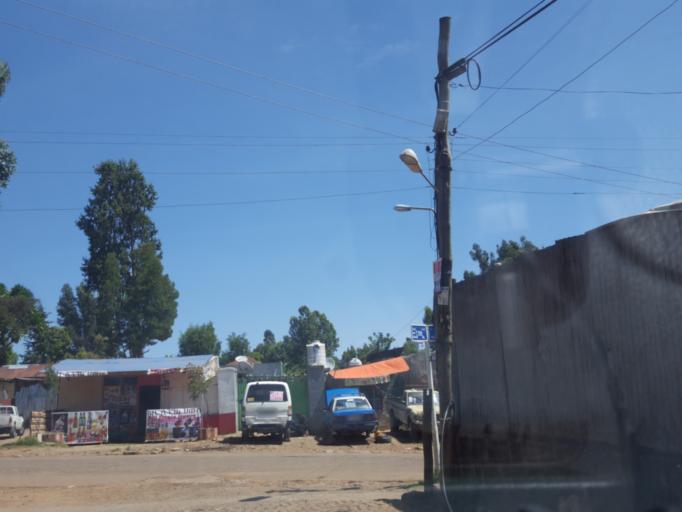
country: ET
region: Adis Abeba
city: Addis Ababa
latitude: 9.0578
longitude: 38.7486
